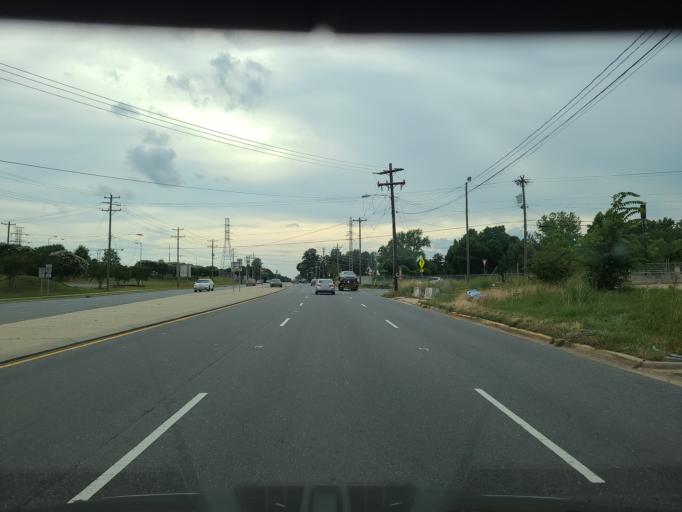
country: US
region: North Carolina
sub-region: Gaston County
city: Belmont
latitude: 35.2353
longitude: -80.9422
